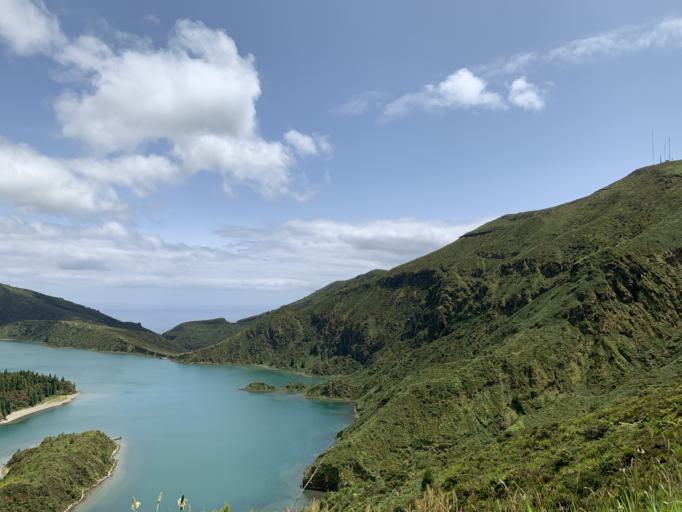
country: PT
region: Azores
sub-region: Vila Franca do Campo
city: Vila Franca do Campo
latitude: 37.7694
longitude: -25.4884
